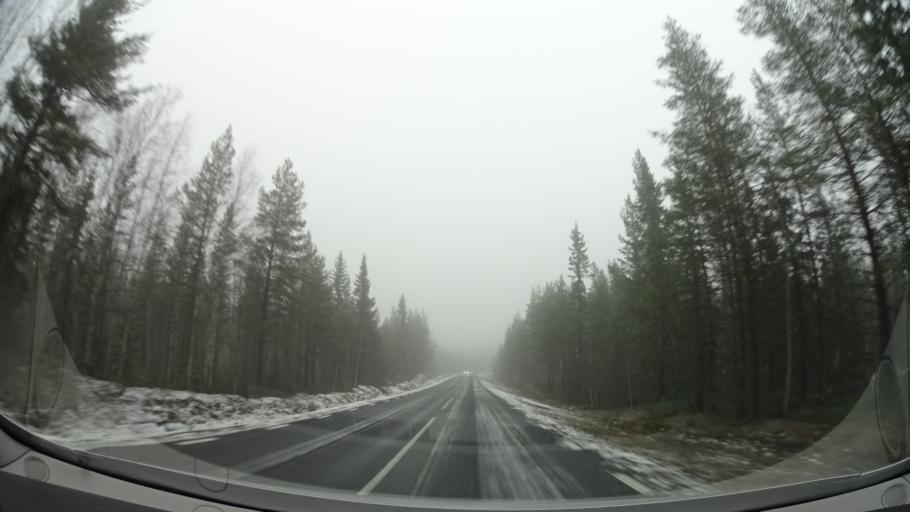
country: SE
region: Vaesterbotten
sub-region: Asele Kommun
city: Insjon
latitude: 64.2295
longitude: 17.5451
